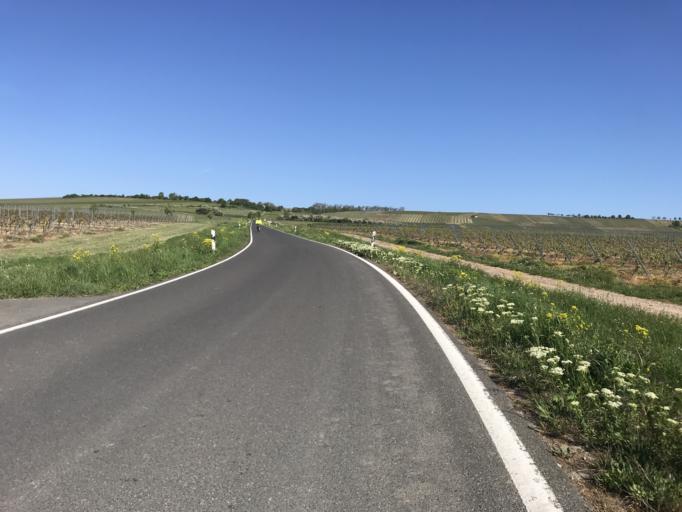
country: DE
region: Rheinland-Pfalz
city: Hahnheim
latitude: 49.8693
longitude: 8.2238
